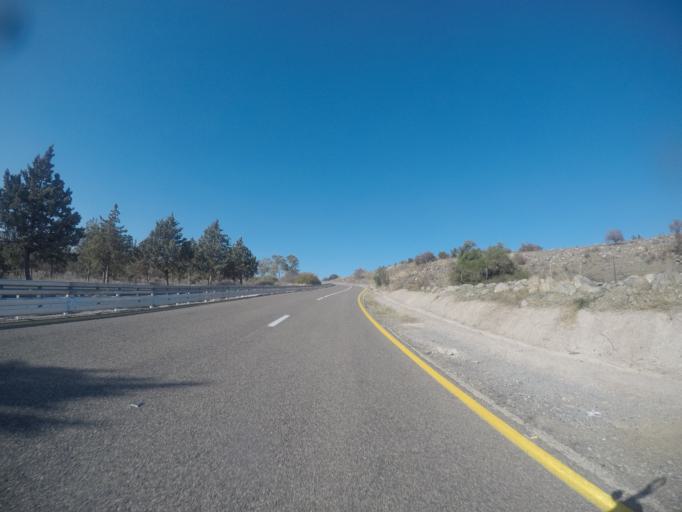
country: JO
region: Irbid
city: Umm Qays
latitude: 32.7069
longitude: 35.6503
